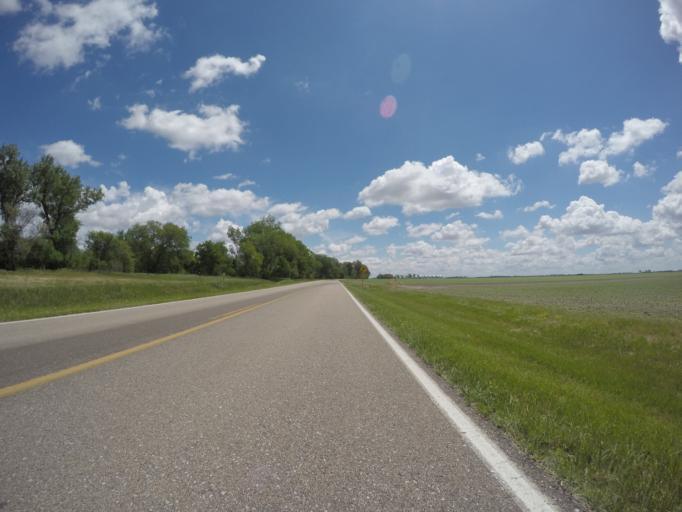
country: US
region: Nebraska
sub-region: Buffalo County
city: Kearney
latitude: 40.6555
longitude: -99.1332
